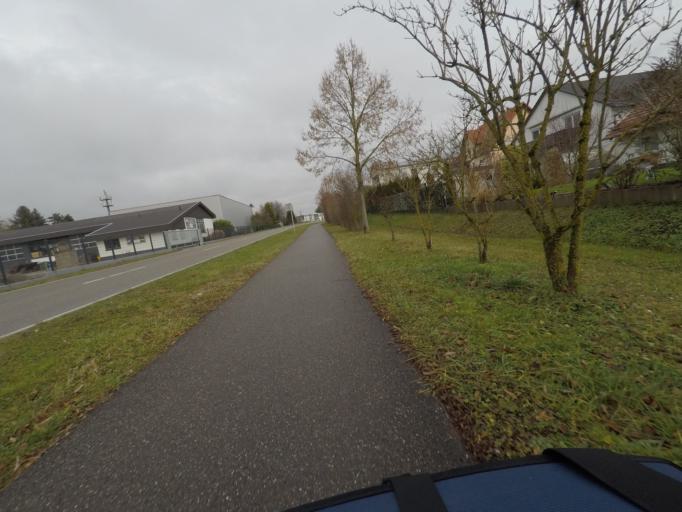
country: DE
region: Baden-Wuerttemberg
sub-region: Karlsruhe Region
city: Au am Rhein
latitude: 48.9473
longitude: 8.2291
